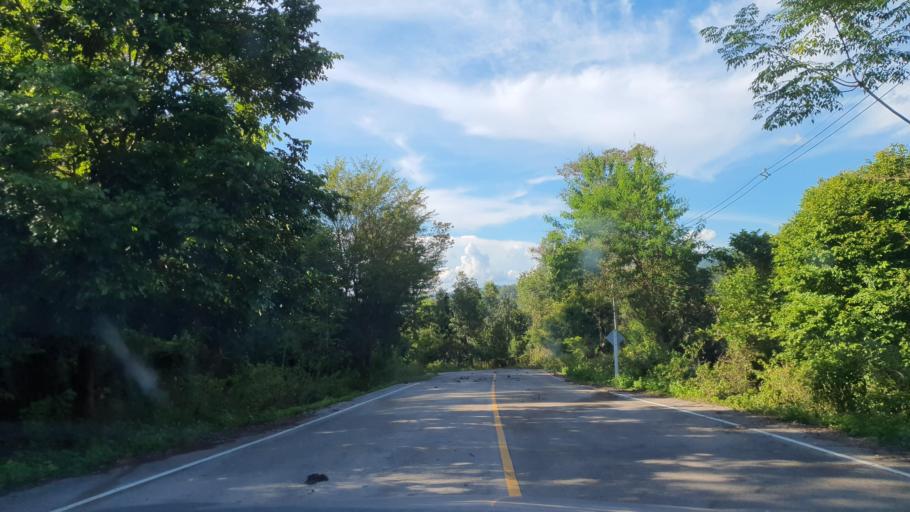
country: TH
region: Chiang Mai
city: Mae On
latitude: 18.7963
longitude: 99.3002
